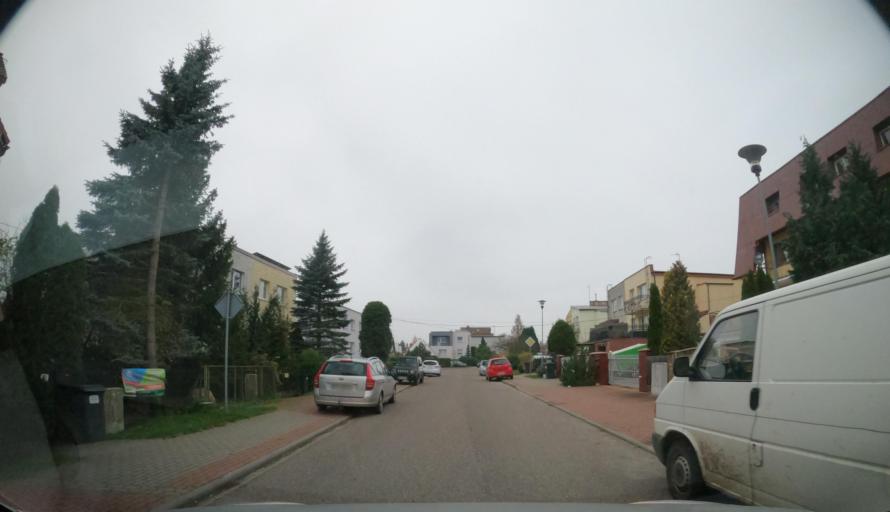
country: PL
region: West Pomeranian Voivodeship
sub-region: Koszalin
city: Koszalin
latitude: 54.1871
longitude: 16.2296
